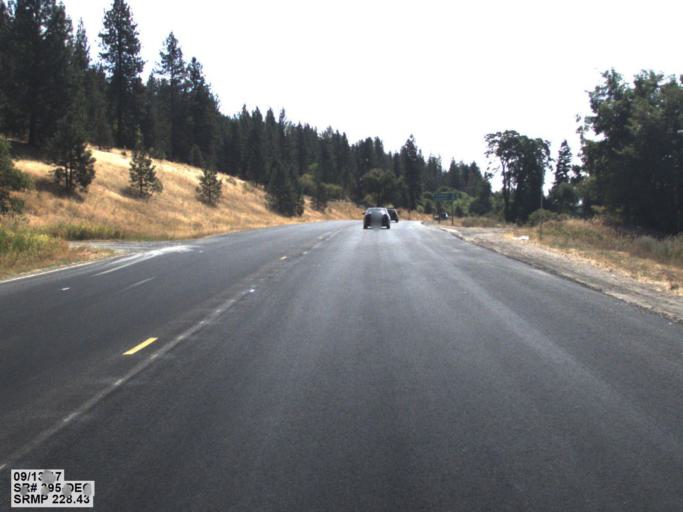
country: US
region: Washington
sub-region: Stevens County
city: Colville
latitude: 48.5293
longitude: -117.9032
